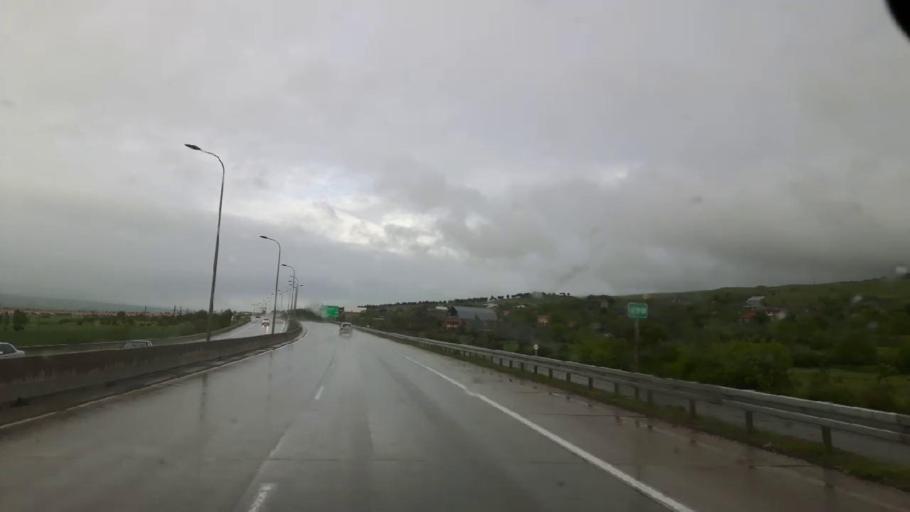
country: GE
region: Shida Kartli
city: Gori
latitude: 42.0240
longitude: 44.2289
